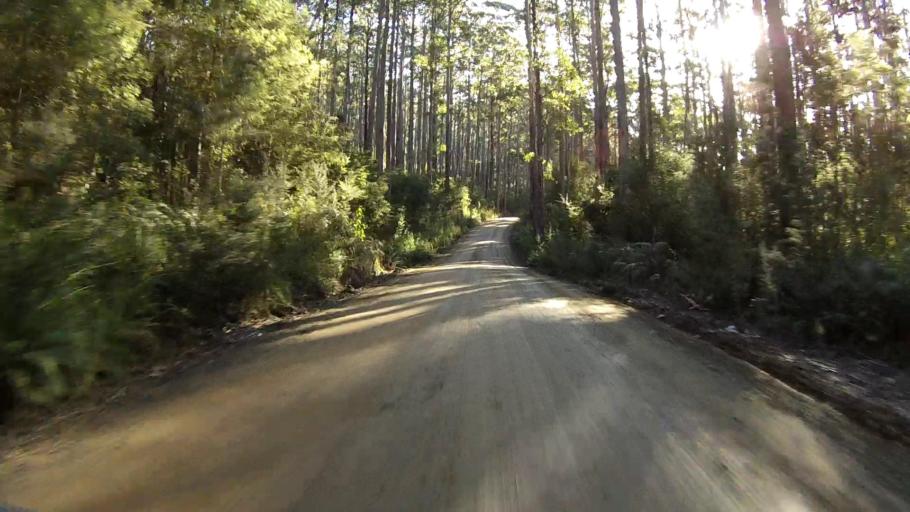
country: AU
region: Tasmania
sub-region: Clarence
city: Sandford
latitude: -43.1241
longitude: 147.9278
